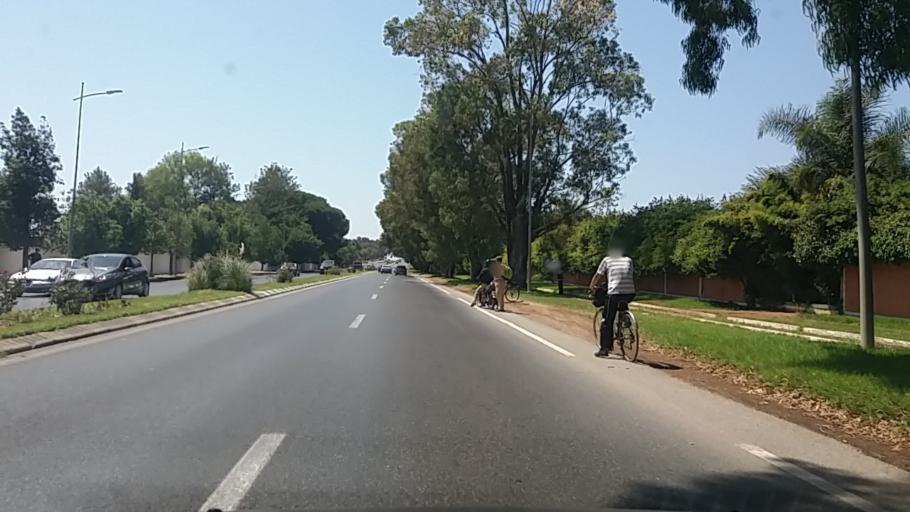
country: MA
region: Rabat-Sale-Zemmour-Zaer
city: Sale
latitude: 34.0300
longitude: -6.7452
